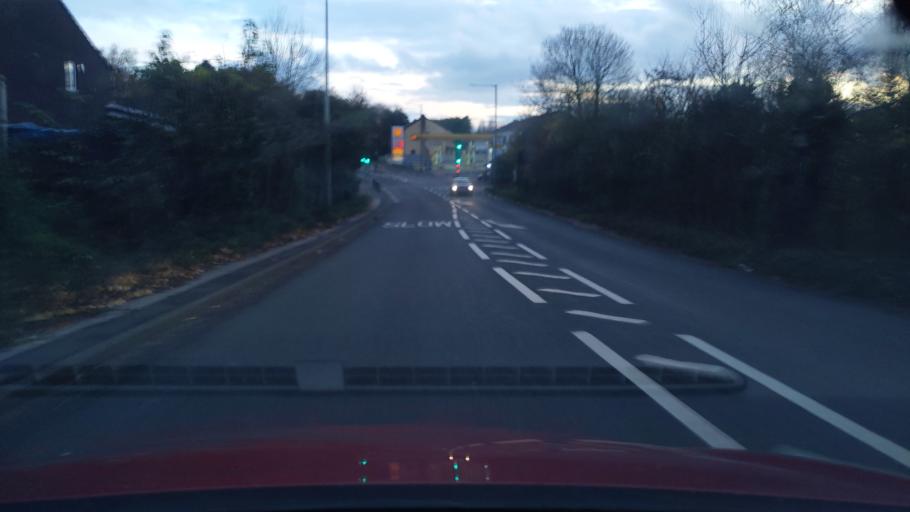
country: GB
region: England
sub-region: Lancashire
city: Clayton-le-Woods
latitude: 53.6935
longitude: -2.6739
